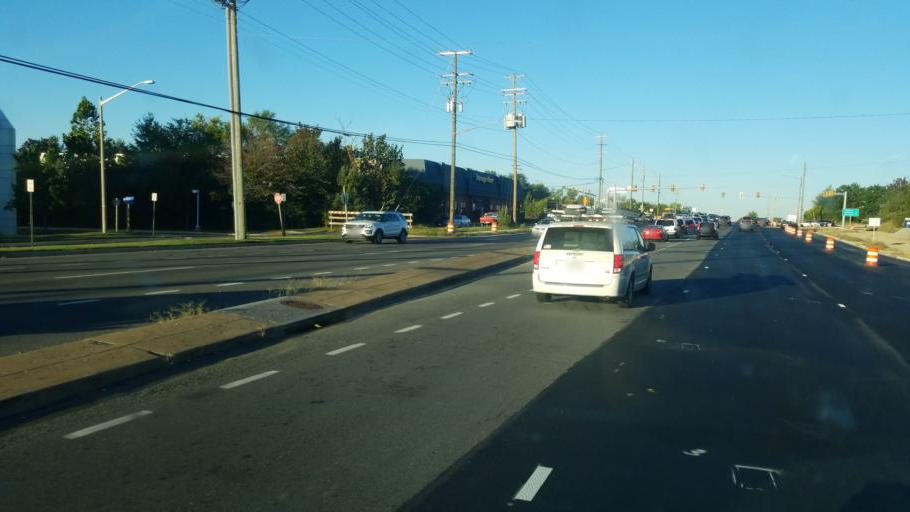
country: US
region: Virginia
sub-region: City of Fairfax
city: Fairfax
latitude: 38.8513
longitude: -77.3361
